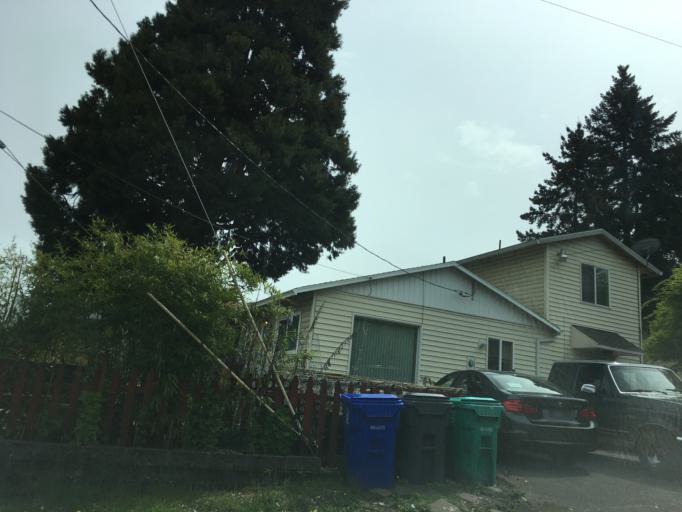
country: US
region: Oregon
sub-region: Multnomah County
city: Lents
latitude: 45.5555
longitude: -122.5702
